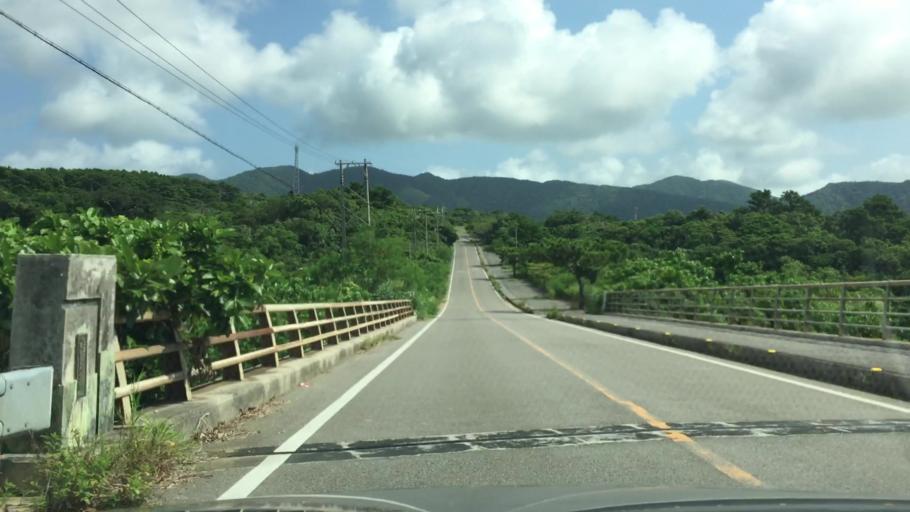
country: JP
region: Okinawa
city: Ishigaki
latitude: 24.4154
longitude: 124.2149
